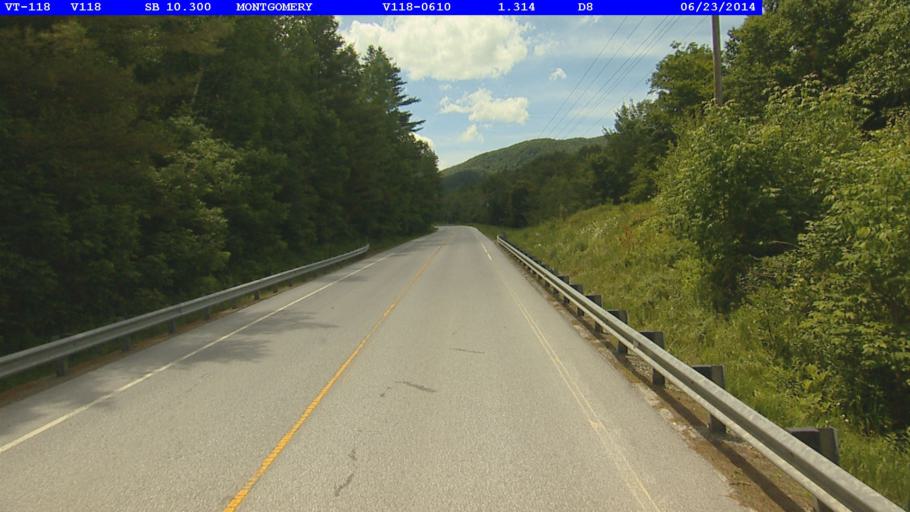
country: US
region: Vermont
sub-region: Franklin County
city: Richford
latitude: 44.8177
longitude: -72.6145
